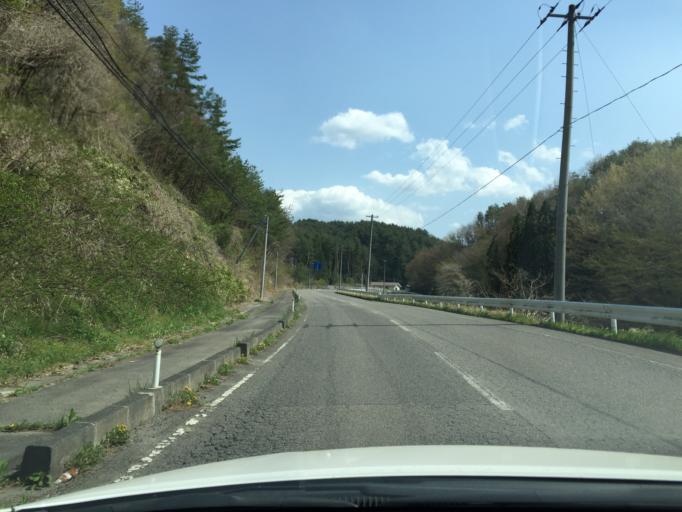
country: JP
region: Fukushima
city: Namie
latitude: 37.4141
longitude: 140.7950
